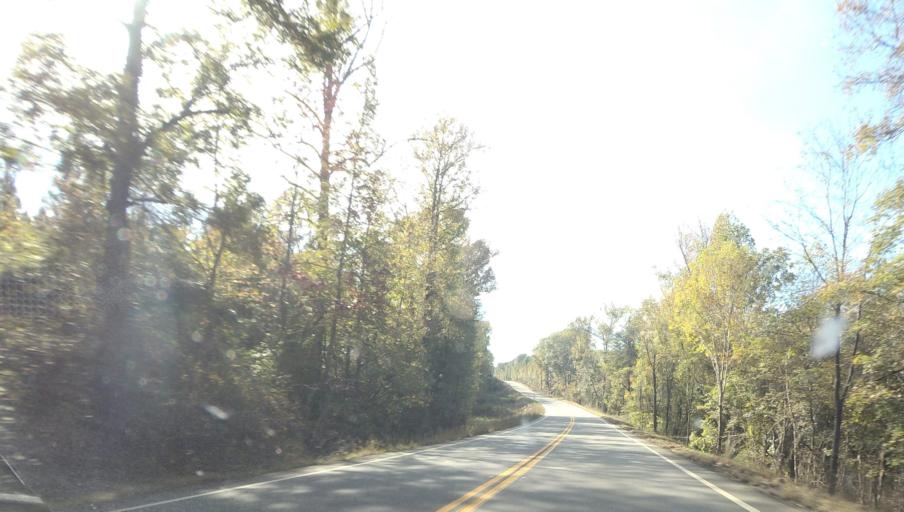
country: US
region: Georgia
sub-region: Taylor County
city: Butler
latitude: 32.7183
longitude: -84.2514
